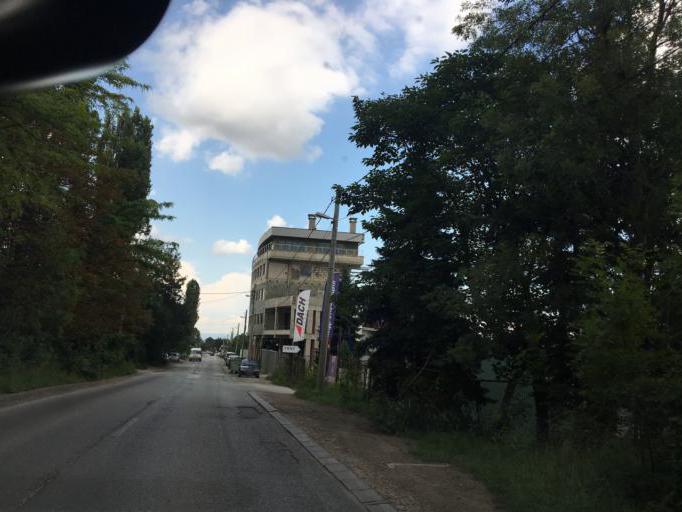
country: BG
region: Sofia-Capital
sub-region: Stolichna Obshtina
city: Sofia
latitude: 42.6333
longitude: 23.3543
